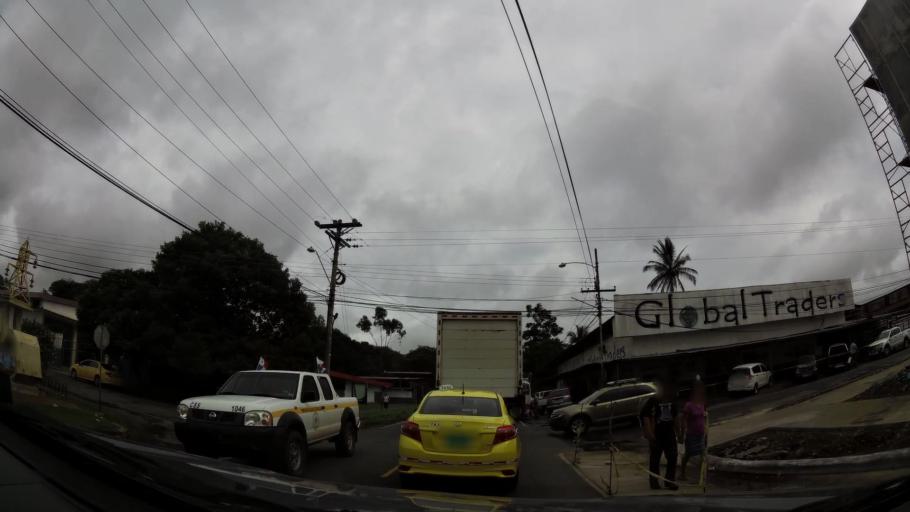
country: PA
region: Chiriqui
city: David
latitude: 8.4312
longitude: -82.4302
